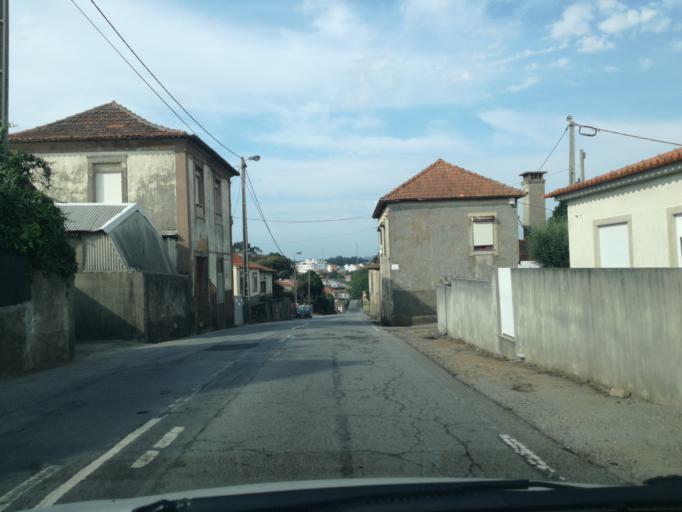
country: PT
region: Aveiro
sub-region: Espinho
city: Espinho
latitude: 41.0196
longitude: -8.6313
